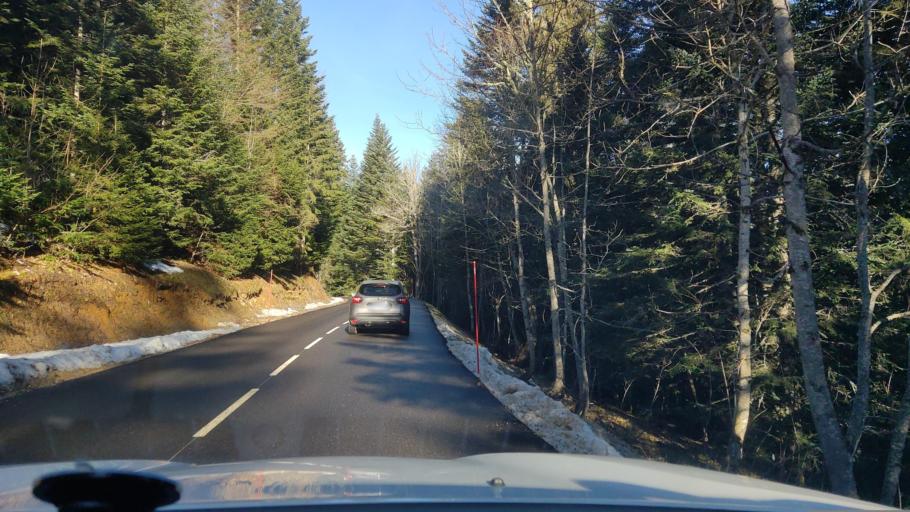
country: FR
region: Rhone-Alpes
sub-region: Departement de la Savoie
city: Mouxy
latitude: 45.6662
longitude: 5.9788
